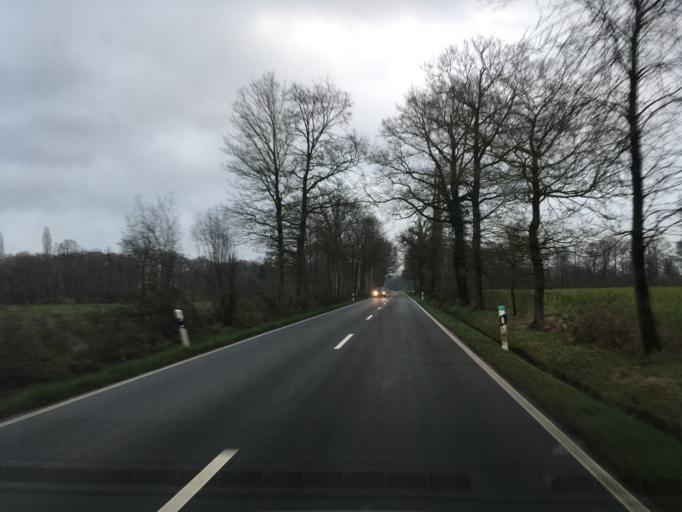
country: DE
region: North Rhine-Westphalia
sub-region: Regierungsbezirk Munster
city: Heek
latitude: 52.1675
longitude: 7.1121
